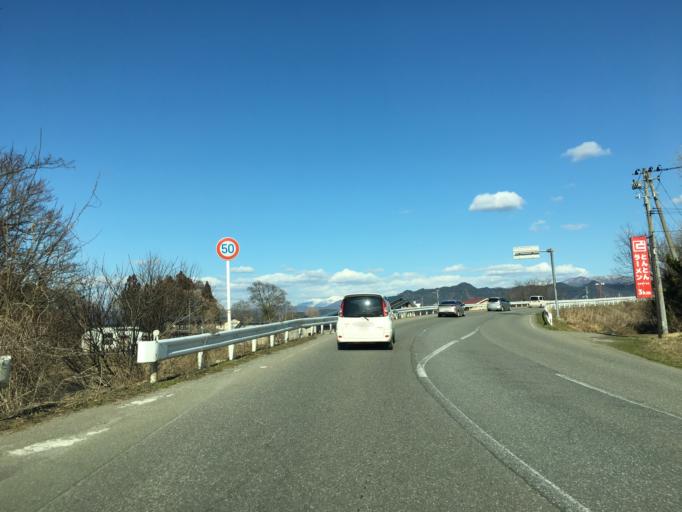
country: JP
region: Yamagata
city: Yonezawa
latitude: 37.9511
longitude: 140.1388
